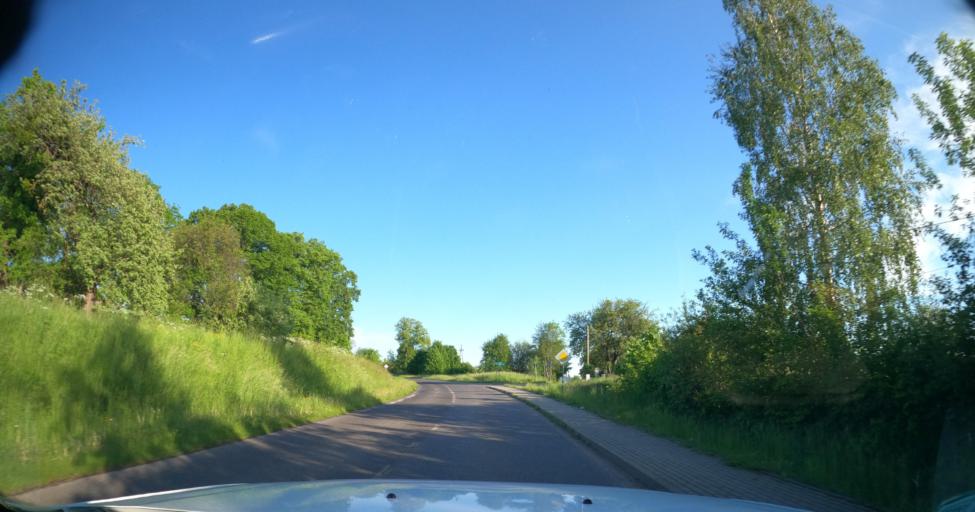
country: PL
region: Warmian-Masurian Voivodeship
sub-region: Powiat braniewski
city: Braniewo
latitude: 54.2690
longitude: 19.9382
